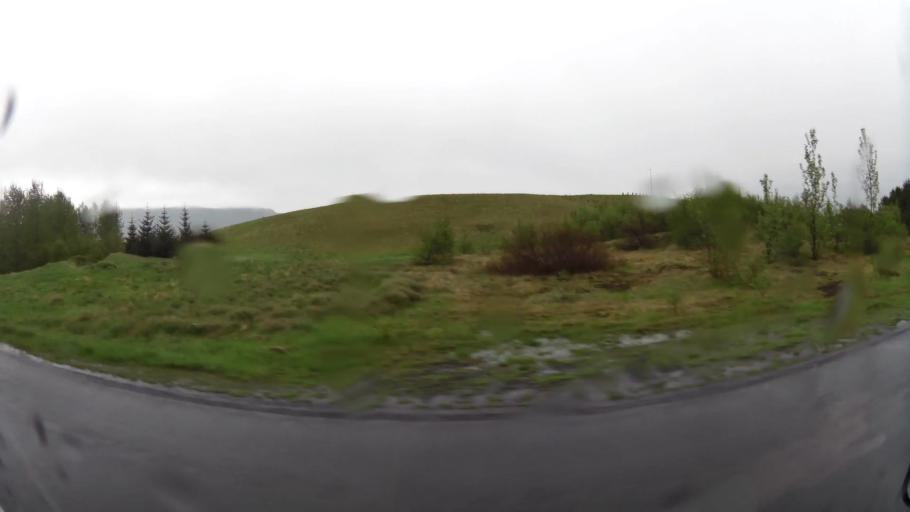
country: IS
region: South
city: Selfoss
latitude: 63.9292
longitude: -20.9926
